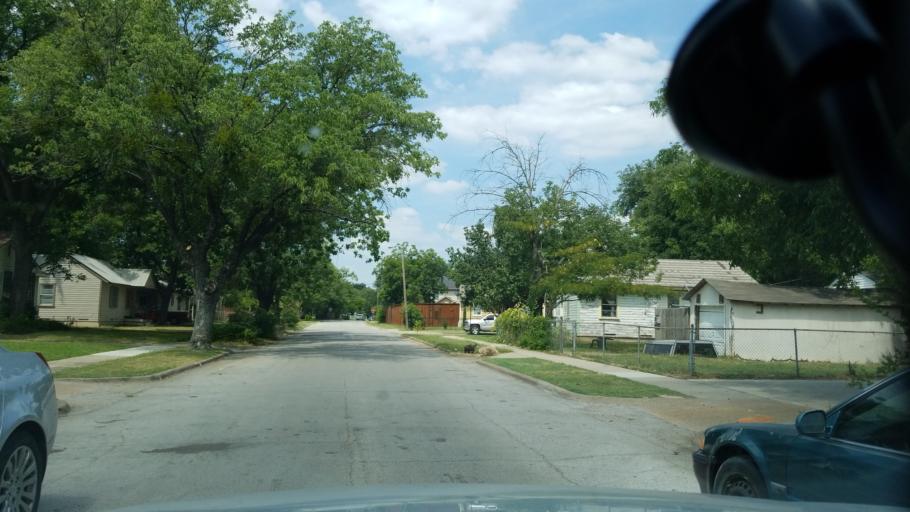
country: US
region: Texas
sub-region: Dallas County
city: Grand Prairie
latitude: 32.7557
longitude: -96.9792
